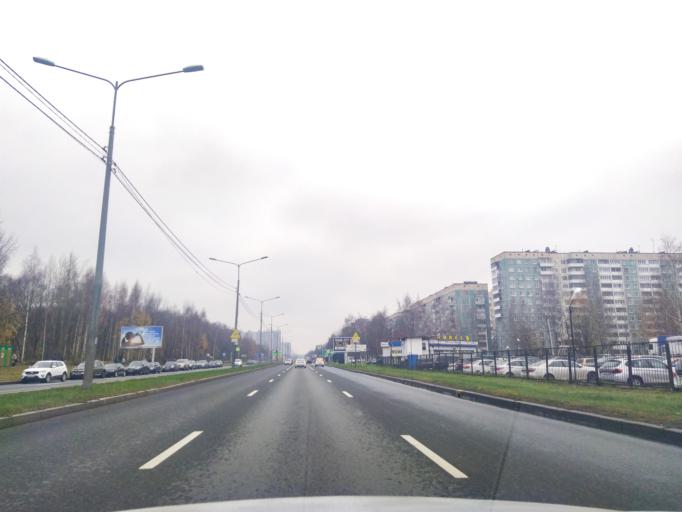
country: RU
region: St.-Petersburg
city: Sosnovka
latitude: 60.0321
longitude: 30.3572
